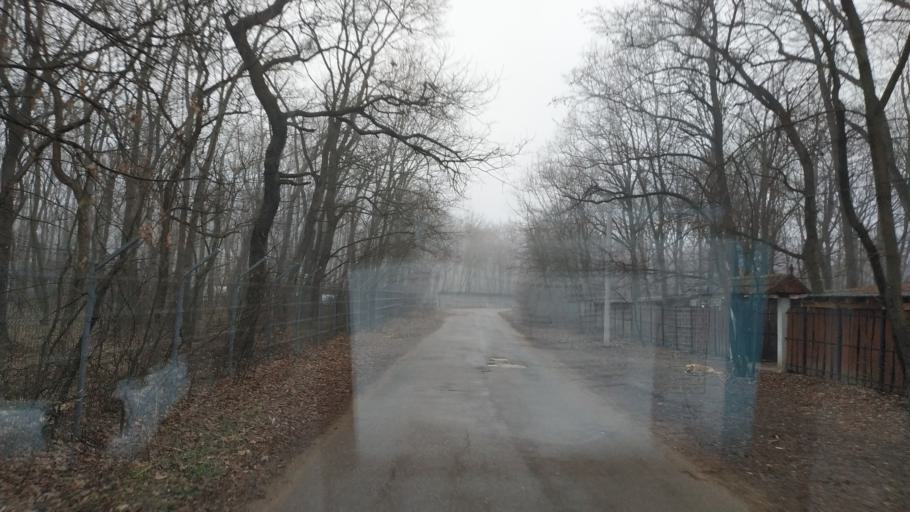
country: MD
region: Laloveni
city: Ialoveni
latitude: 46.9508
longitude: 28.6999
